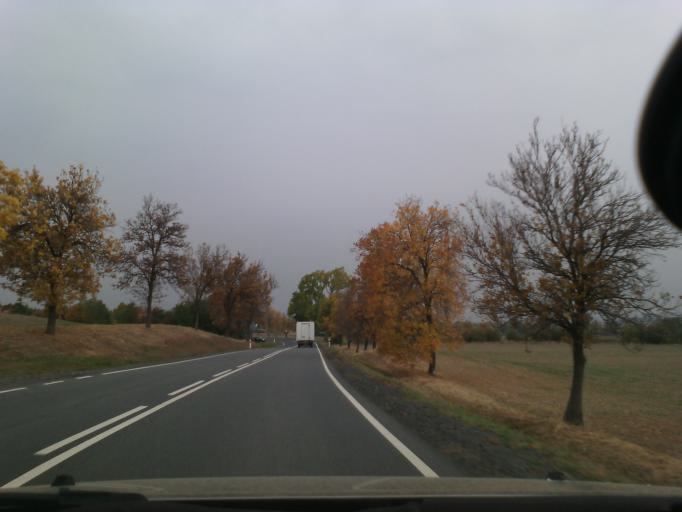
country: PL
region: Lower Silesian Voivodeship
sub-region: Powiat swidnicki
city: Swiebodzice
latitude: 50.8854
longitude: 16.2703
